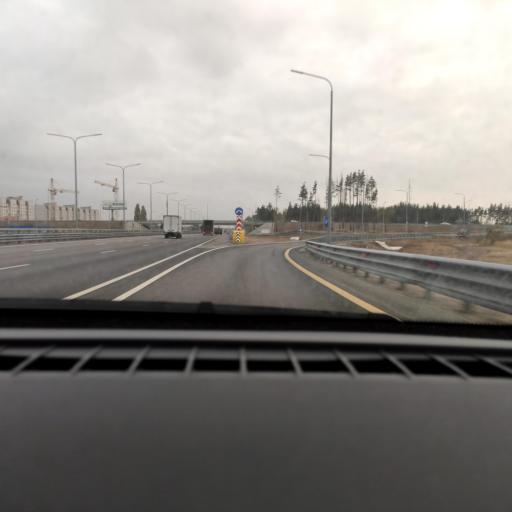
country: RU
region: Voronezj
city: Somovo
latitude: 51.7445
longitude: 39.3063
